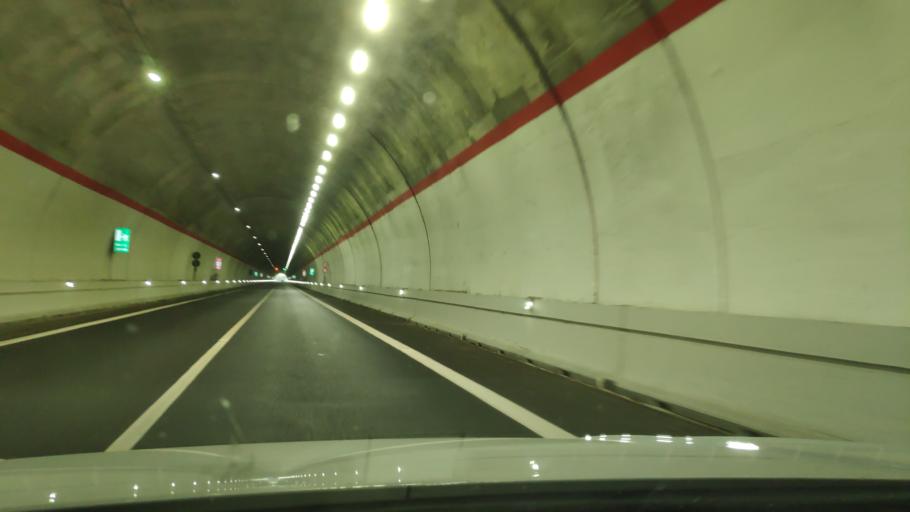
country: IT
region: Calabria
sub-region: Provincia di Reggio Calabria
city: Palizzi Marina
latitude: 37.9245
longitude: 15.9997
